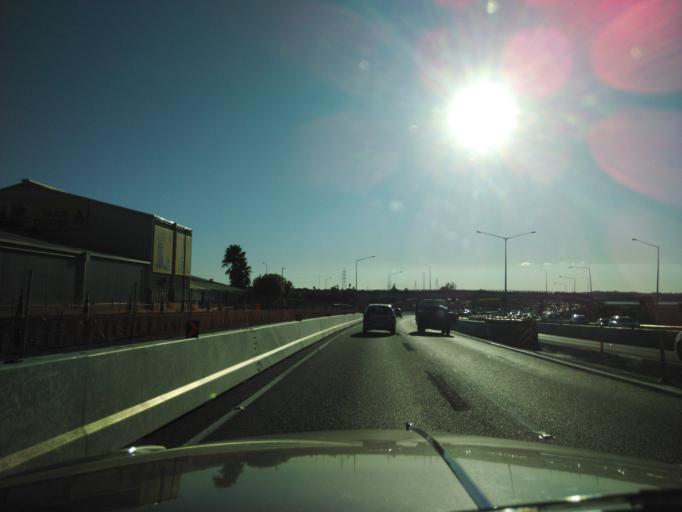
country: NZ
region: Auckland
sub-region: Auckland
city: Rosebank
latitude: -36.8671
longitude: 174.6682
